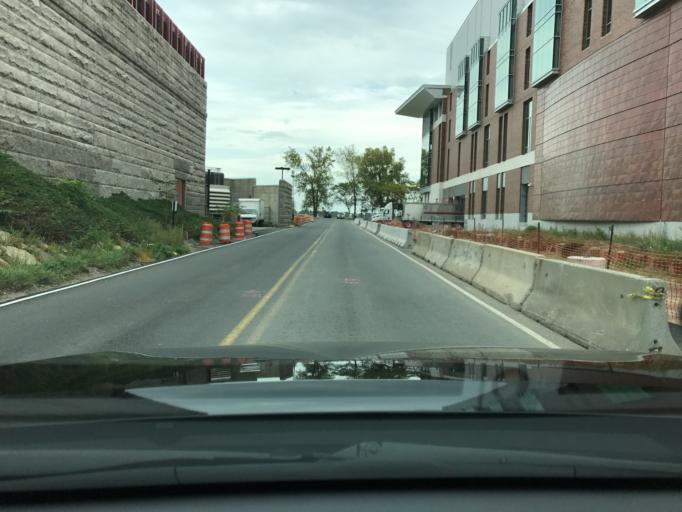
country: US
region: Massachusetts
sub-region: Suffolk County
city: South Boston
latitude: 42.3139
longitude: -71.0355
